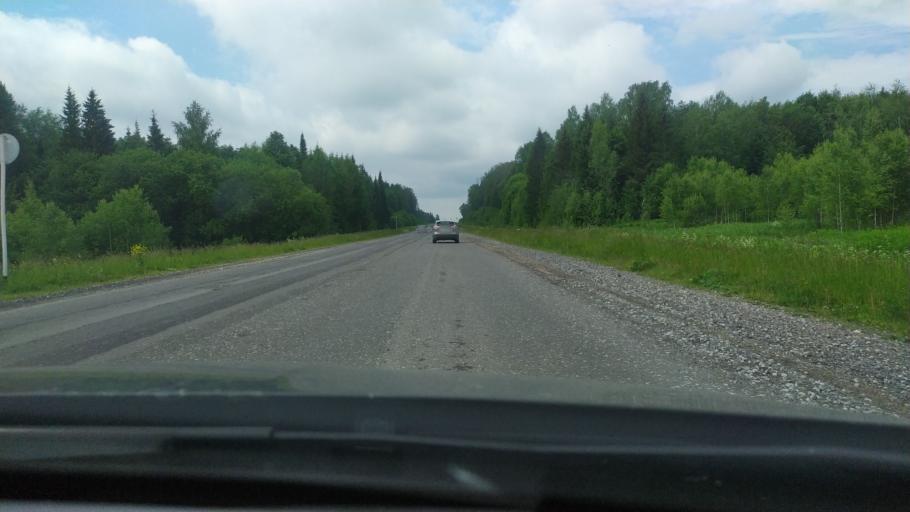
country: RU
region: Perm
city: Kalino
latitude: 58.2722
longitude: 57.3786
